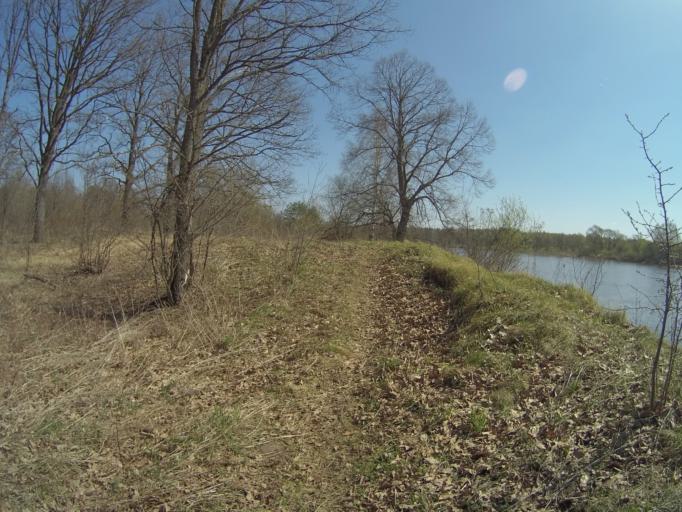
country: RU
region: Vladimir
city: Raduzhnyy
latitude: 56.0509
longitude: 40.3302
